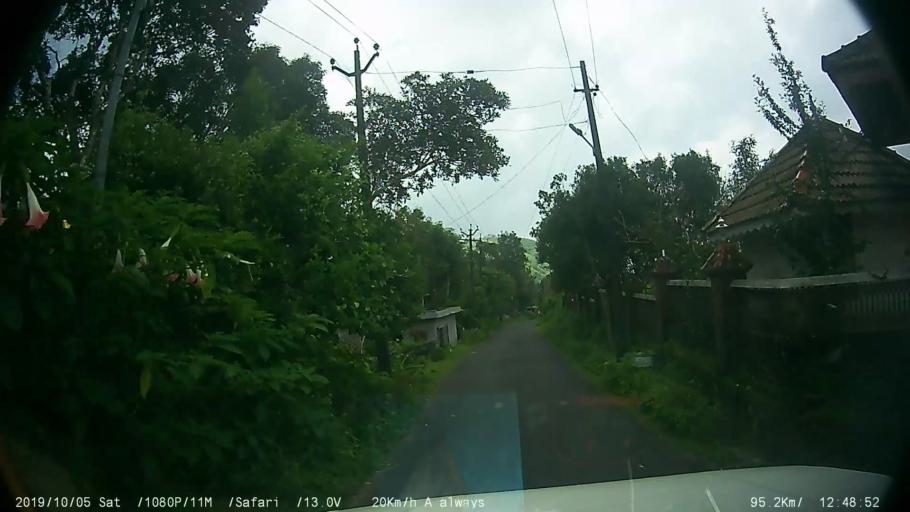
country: IN
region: Kerala
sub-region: Kottayam
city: Erattupetta
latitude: 9.5767
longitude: 76.9710
